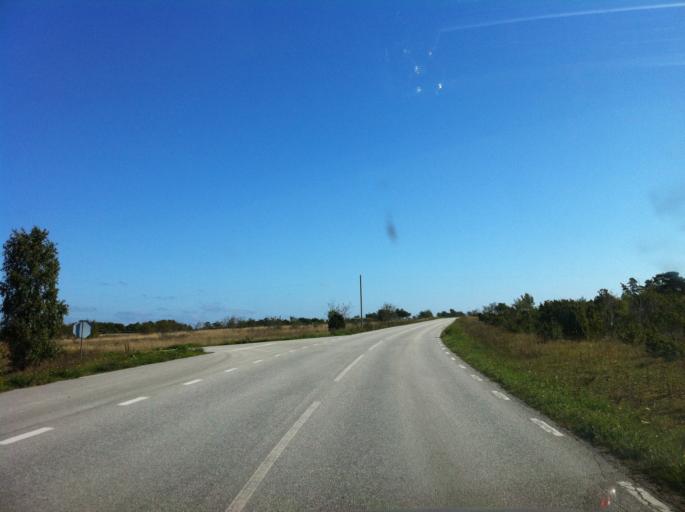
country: SE
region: Gotland
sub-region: Gotland
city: Slite
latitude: 57.9352
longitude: 19.1785
